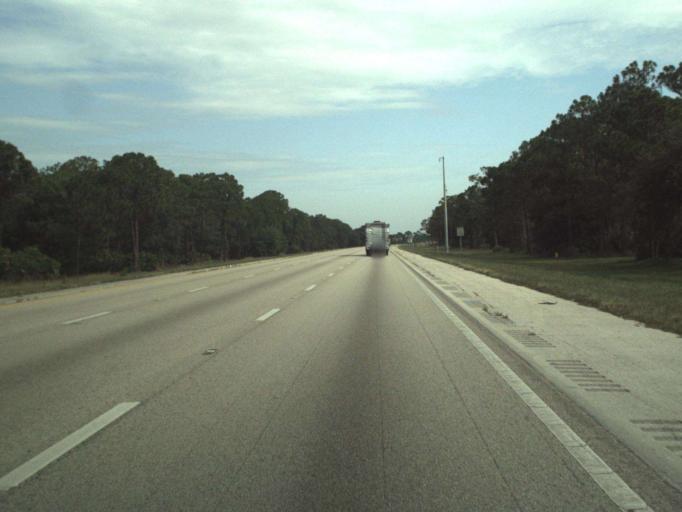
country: US
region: Florida
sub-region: Martin County
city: Palm City
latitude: 27.1715
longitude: -80.3934
